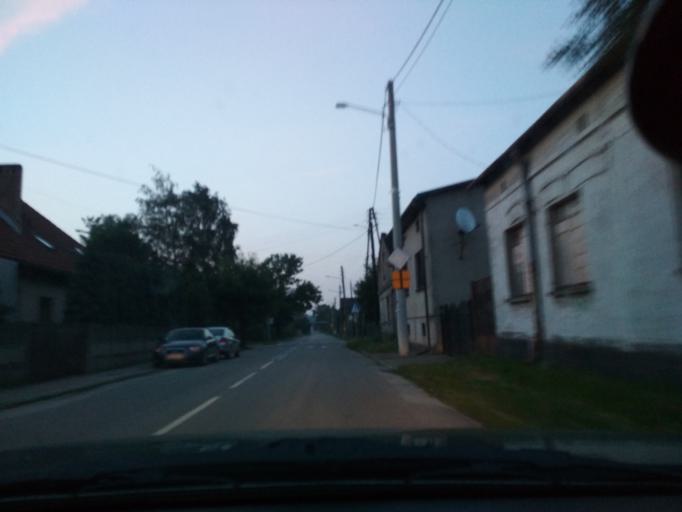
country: PL
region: Silesian Voivodeship
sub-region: Powiat zawiercianski
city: Zawiercie
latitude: 50.4848
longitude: 19.4401
